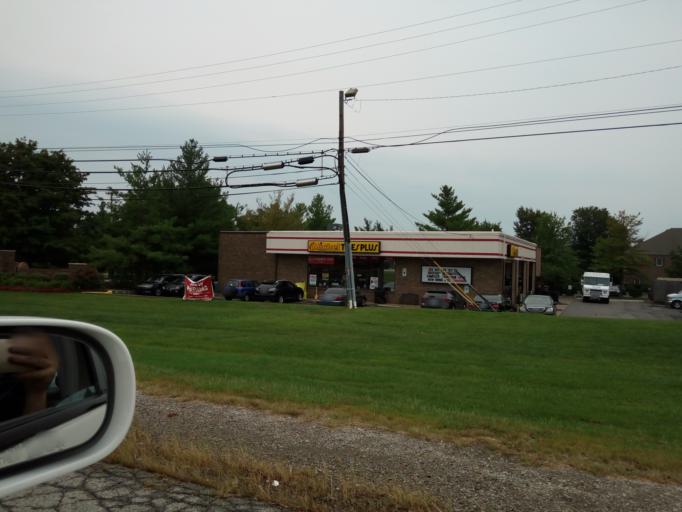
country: US
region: Kentucky
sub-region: Jefferson County
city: Middletown
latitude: 38.2435
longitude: -85.5190
